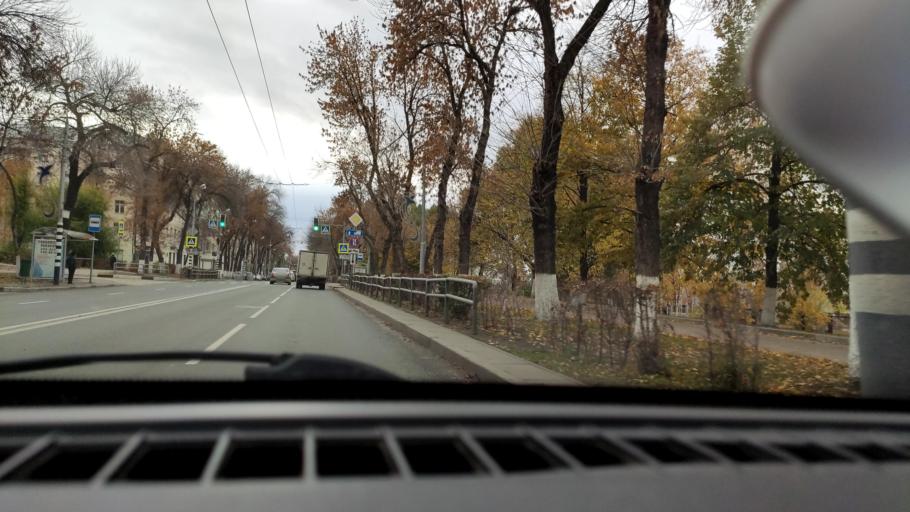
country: RU
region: Samara
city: Samara
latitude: 53.2089
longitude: 50.1170
